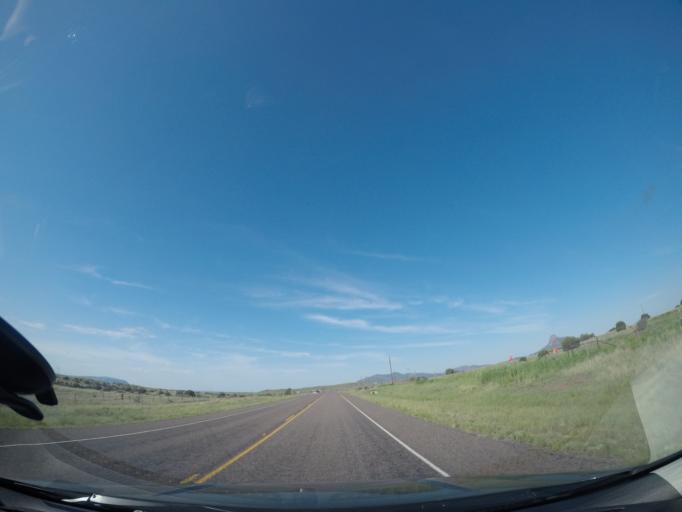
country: US
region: Texas
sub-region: Brewster County
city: Alpine
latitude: 30.2041
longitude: -103.5766
